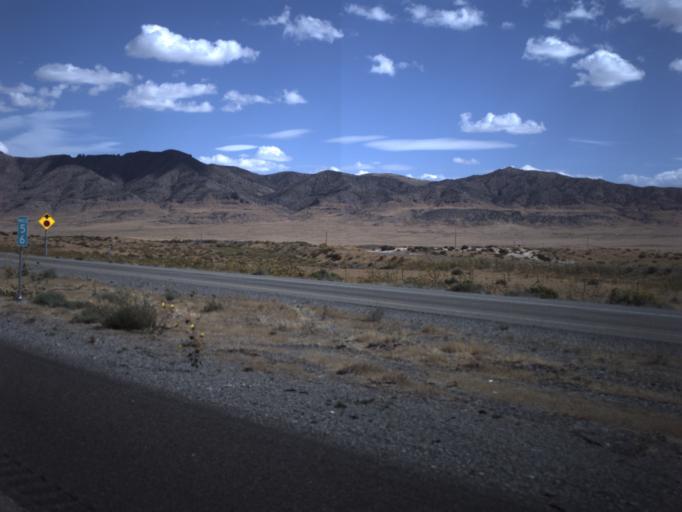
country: US
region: Utah
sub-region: Tooele County
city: Grantsville
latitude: 40.7666
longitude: -112.9877
